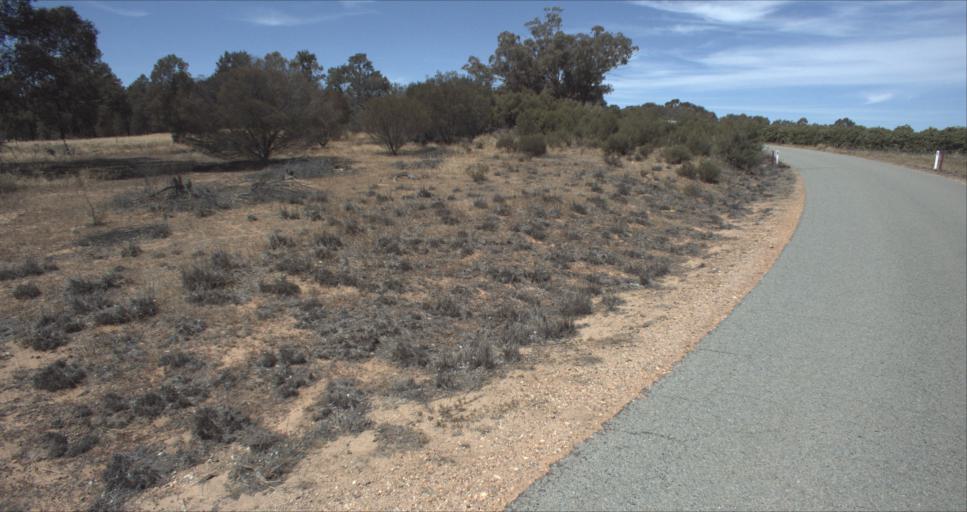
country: AU
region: New South Wales
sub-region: Leeton
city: Leeton
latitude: -34.6749
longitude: 146.4329
